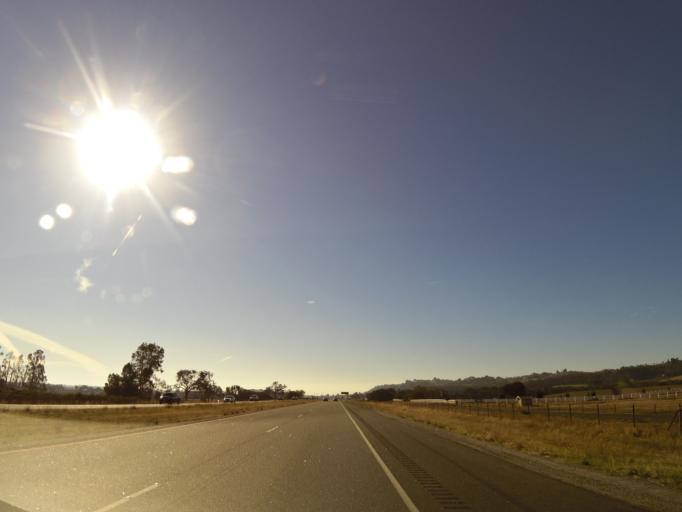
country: US
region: California
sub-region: San Luis Obispo County
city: Paso Robles
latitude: 35.6752
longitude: -120.6967
